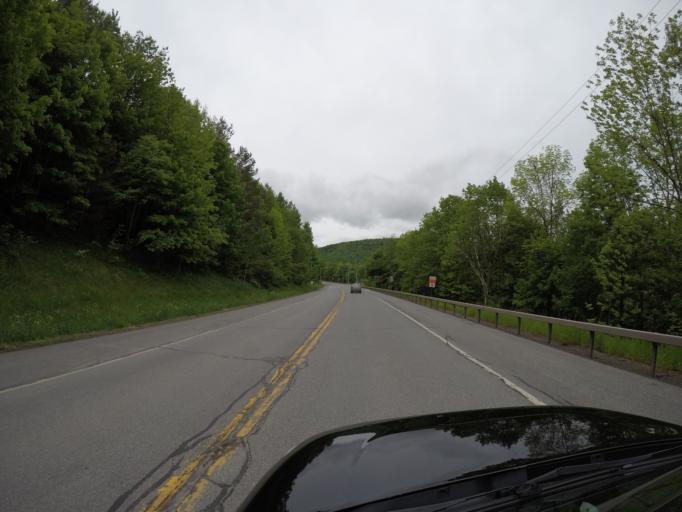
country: US
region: New York
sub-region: Delaware County
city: Stamford
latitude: 42.1477
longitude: -74.6447
